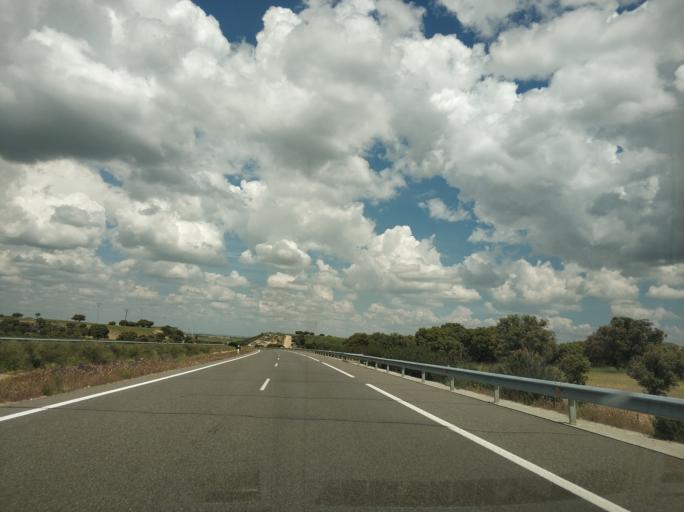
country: ES
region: Castille and Leon
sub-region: Provincia de Salamanca
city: Mozarbez
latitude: 40.8388
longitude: -5.6376
